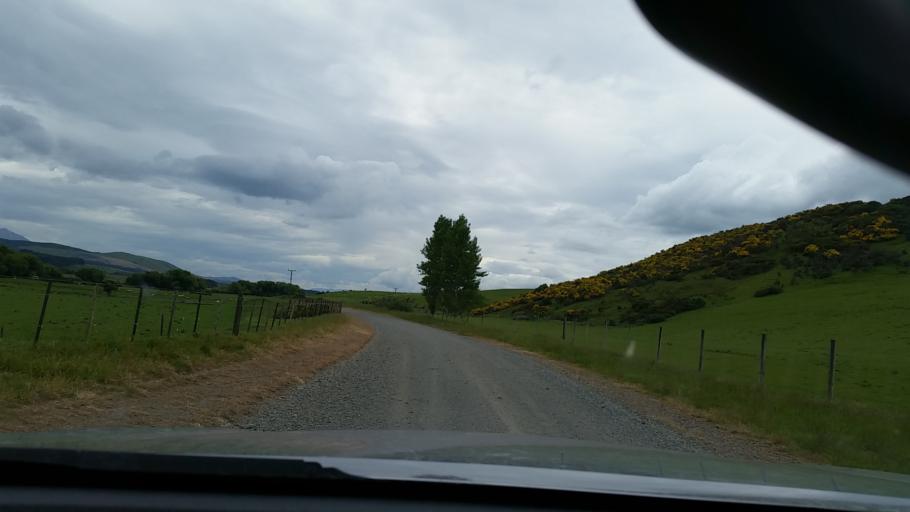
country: NZ
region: Southland
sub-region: Southland District
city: Winton
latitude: -45.8333
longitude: 168.1480
